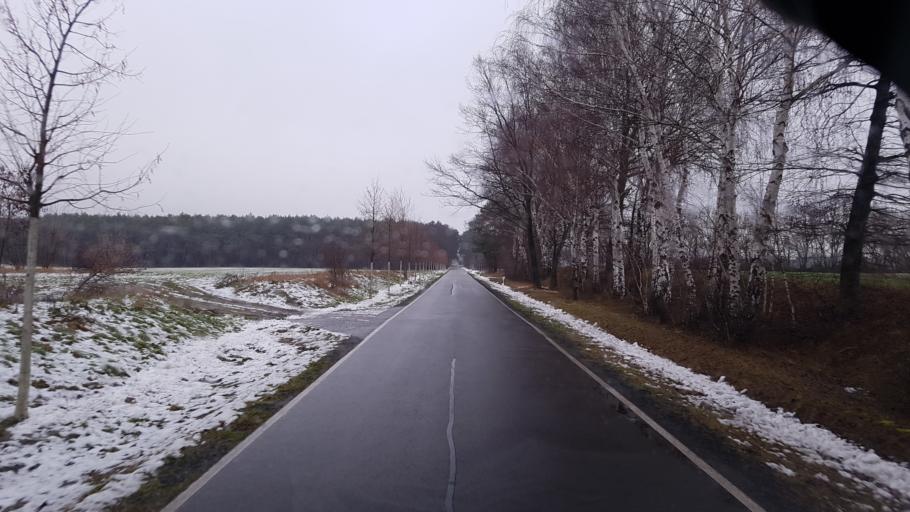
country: DE
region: Brandenburg
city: Neu Zauche
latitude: 51.9370
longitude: 14.1034
